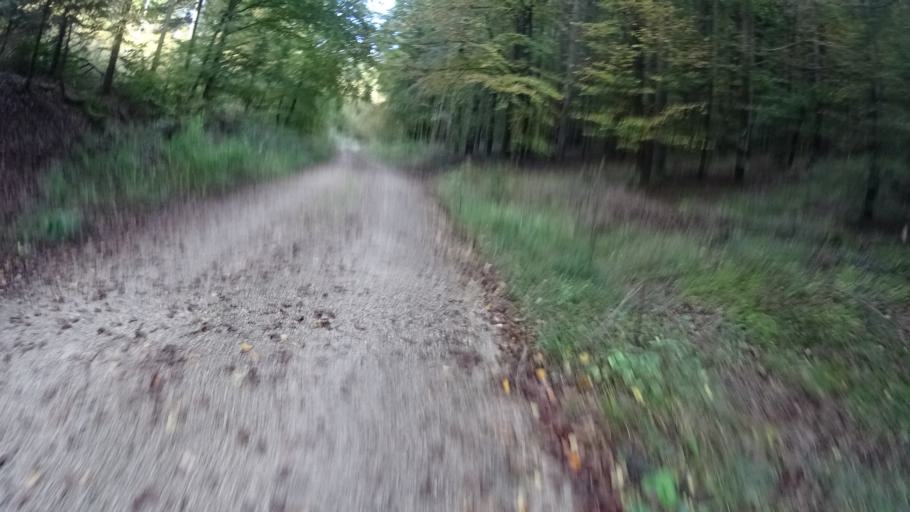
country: DE
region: Bavaria
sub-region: Upper Bavaria
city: Walting
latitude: 48.9025
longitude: 11.3152
